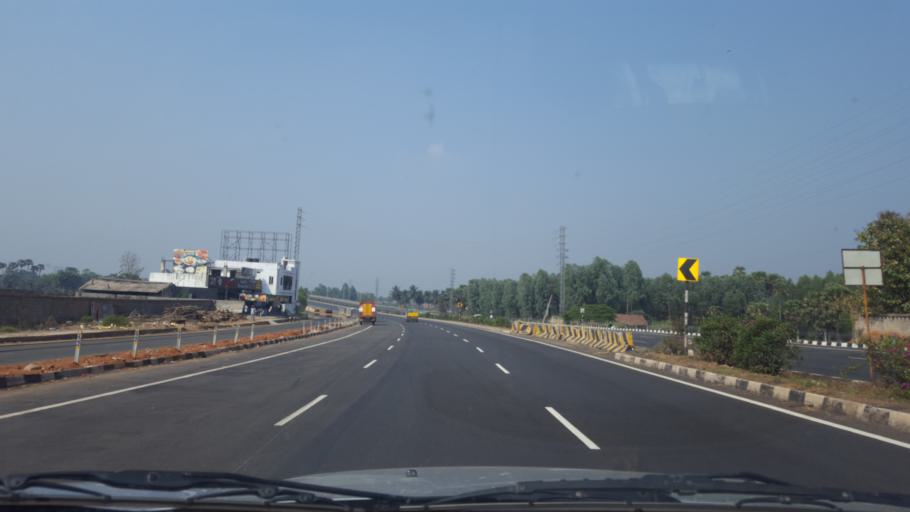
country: IN
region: Andhra Pradesh
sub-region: Vishakhapatnam
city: Bhimunipatnam
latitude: 17.9638
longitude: 83.4255
